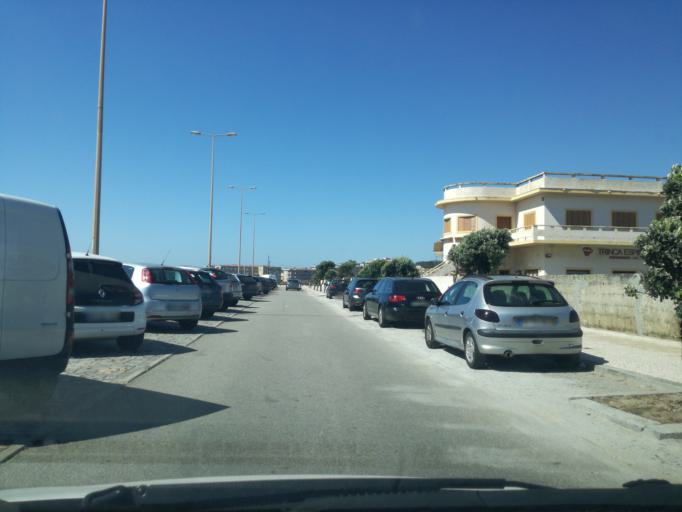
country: PT
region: Porto
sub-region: Matosinhos
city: Lavra
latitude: 41.2677
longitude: -8.7262
